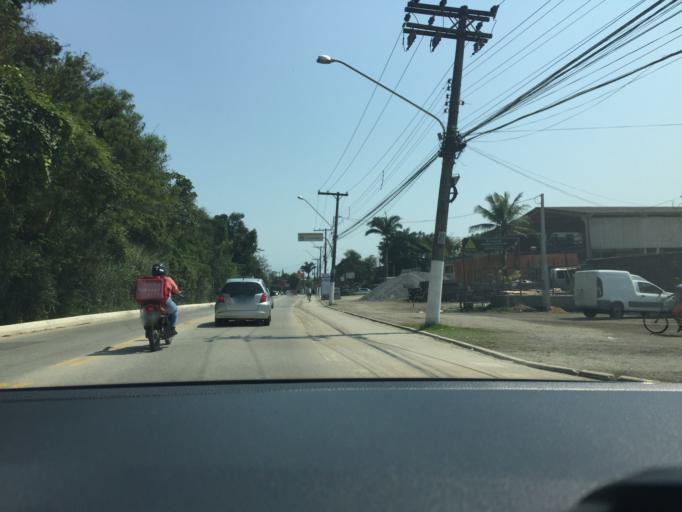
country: BR
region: Sao Paulo
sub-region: Guaruja
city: Guaruja
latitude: -23.9805
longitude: -46.1942
